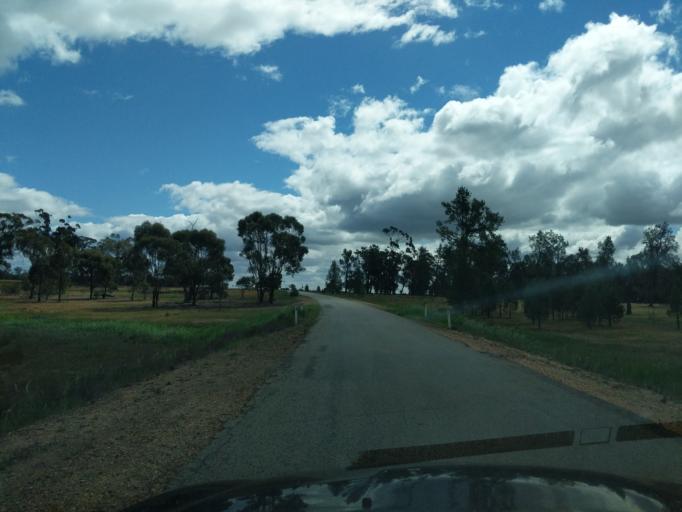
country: AU
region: New South Wales
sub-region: Coolamon
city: Coolamon
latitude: -34.8709
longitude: 146.9008
